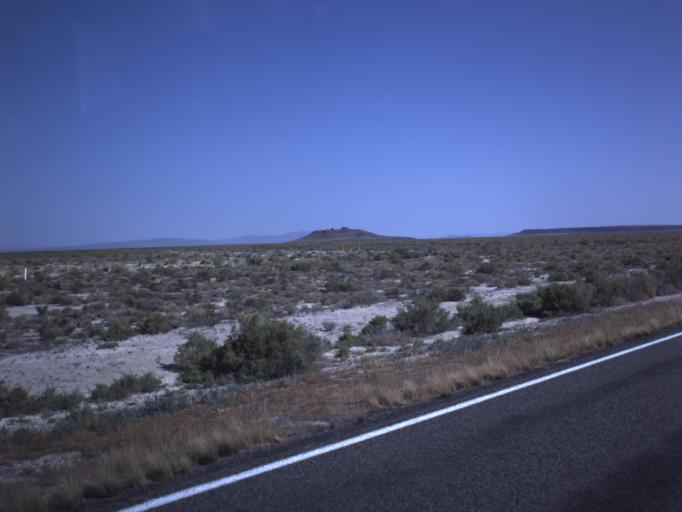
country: US
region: Utah
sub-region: Millard County
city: Delta
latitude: 39.0855
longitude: -112.7534
